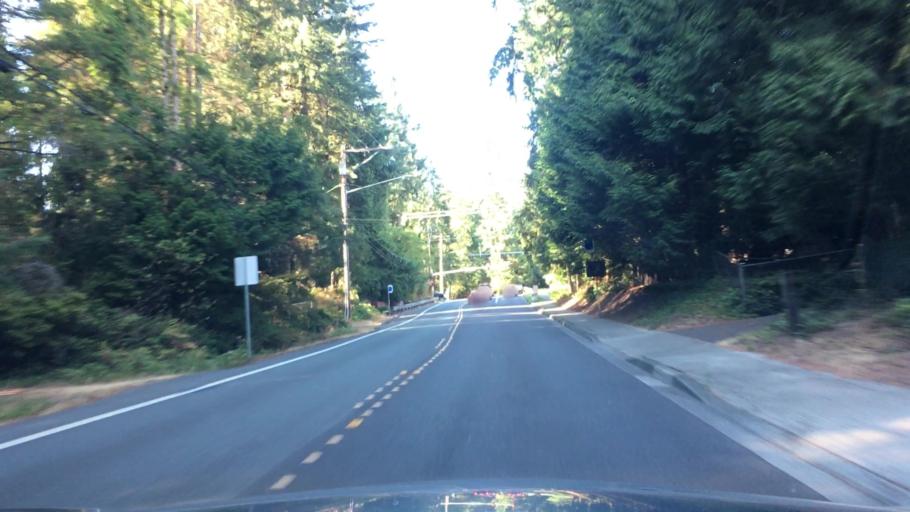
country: US
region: Washington
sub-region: Snohomish County
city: North Creek
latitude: 47.7899
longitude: -122.1864
